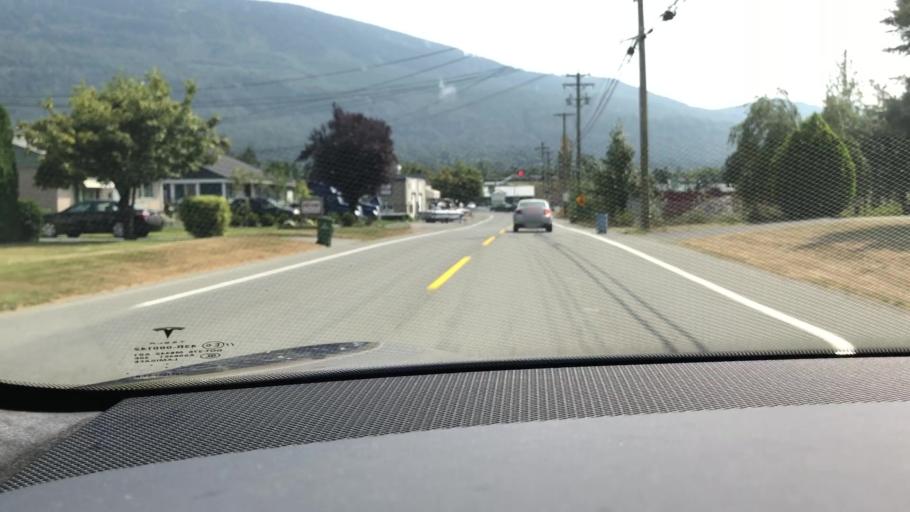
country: CA
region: British Columbia
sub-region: Fraser Valley Regional District
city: Chilliwack
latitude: 49.0833
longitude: -122.0649
